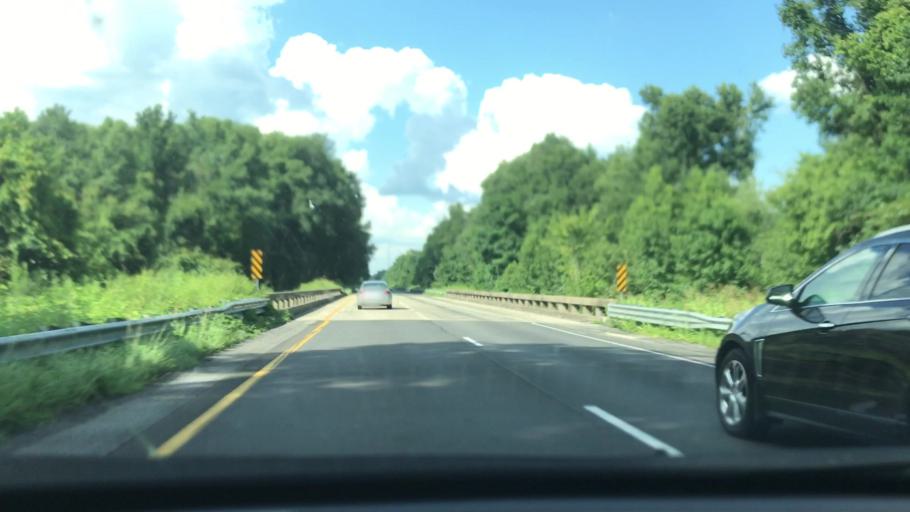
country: US
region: South Carolina
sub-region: Clarendon County
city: Manning
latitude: 33.8329
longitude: -80.1311
